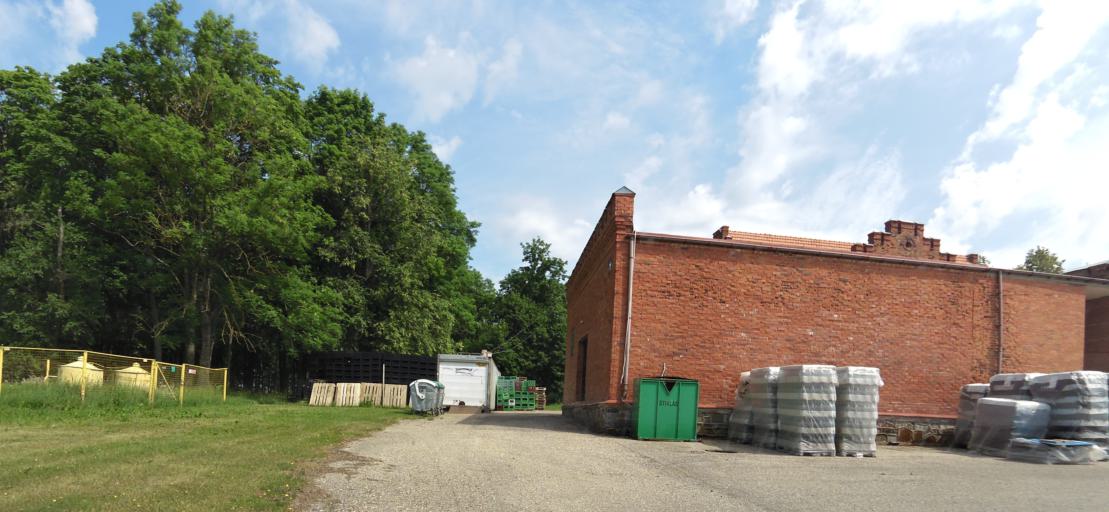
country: LT
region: Panevezys
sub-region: Birzai
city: Birzai
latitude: 56.2885
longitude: 24.6036
